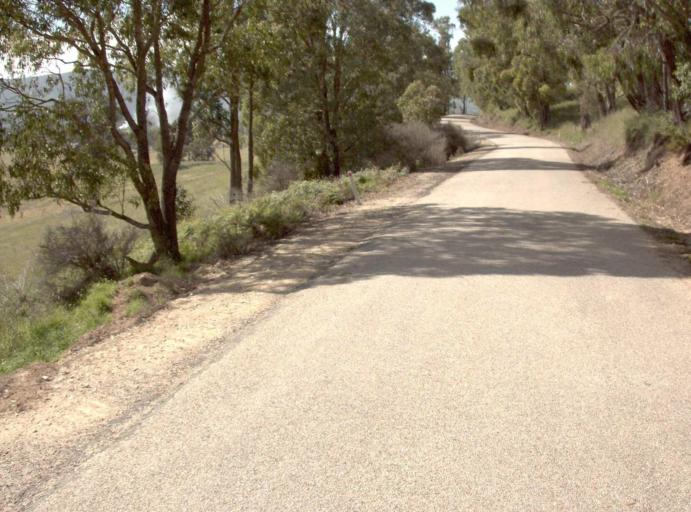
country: AU
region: Victoria
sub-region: East Gippsland
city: Lakes Entrance
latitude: -37.5165
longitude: 148.1417
